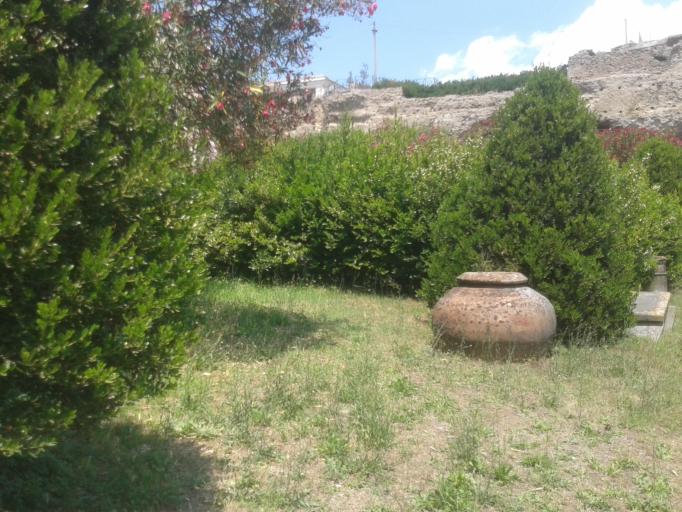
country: IT
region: Campania
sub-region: Provincia di Napoli
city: Pompei
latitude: 40.7478
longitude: 14.4841
